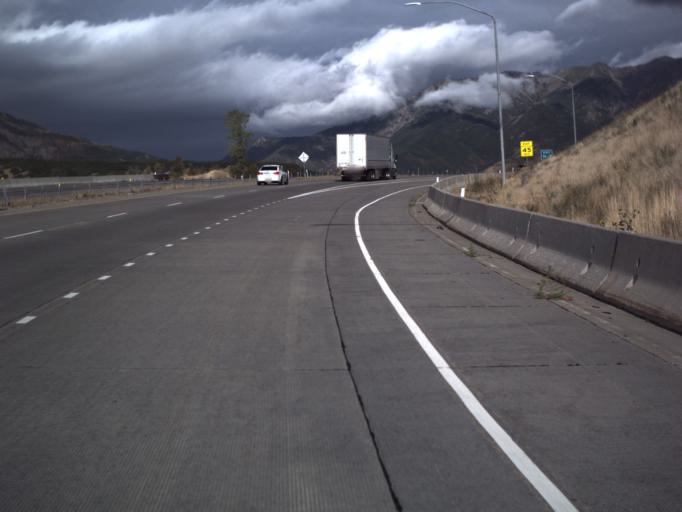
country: US
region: Utah
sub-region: Morgan County
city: Mountain Green
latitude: 41.1126
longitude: -111.7598
